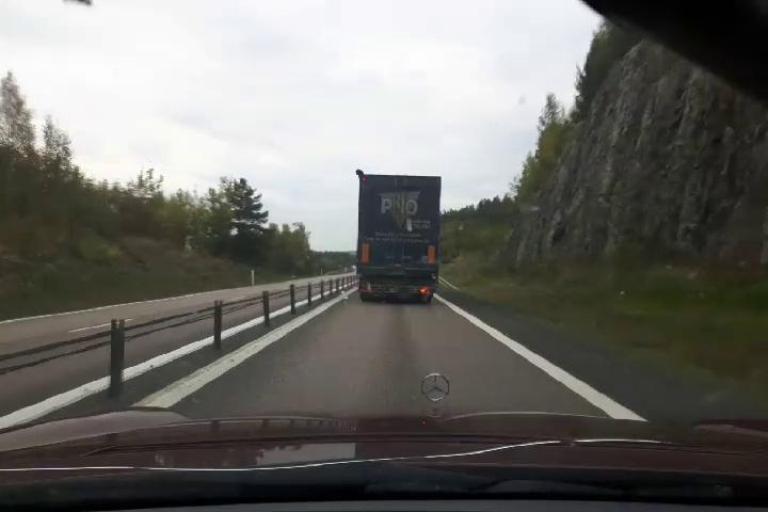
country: SE
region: Vaesternorrland
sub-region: Haernoesands Kommun
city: Haernoesand
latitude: 62.8262
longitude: 17.9690
